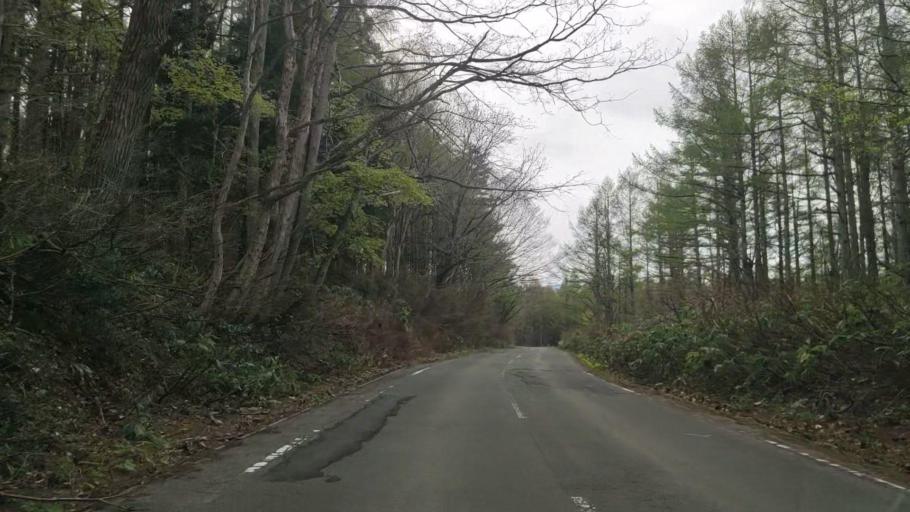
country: JP
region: Aomori
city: Aomori Shi
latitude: 40.7300
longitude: 140.8453
